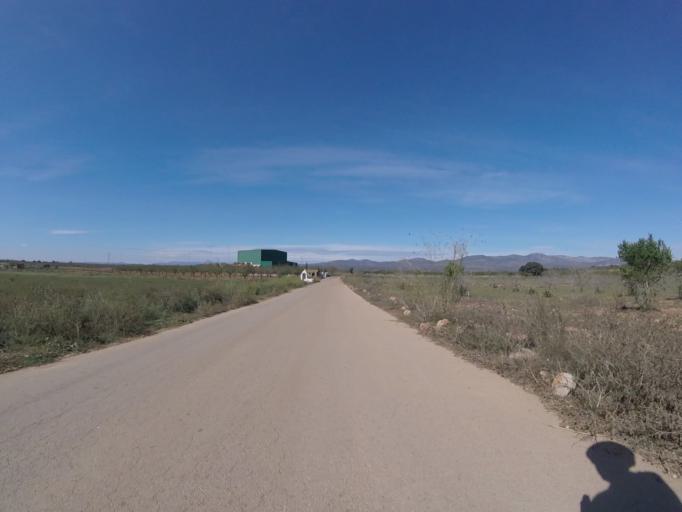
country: ES
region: Valencia
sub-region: Provincia de Castello
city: Benlloch
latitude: 40.2057
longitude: 0.0492
